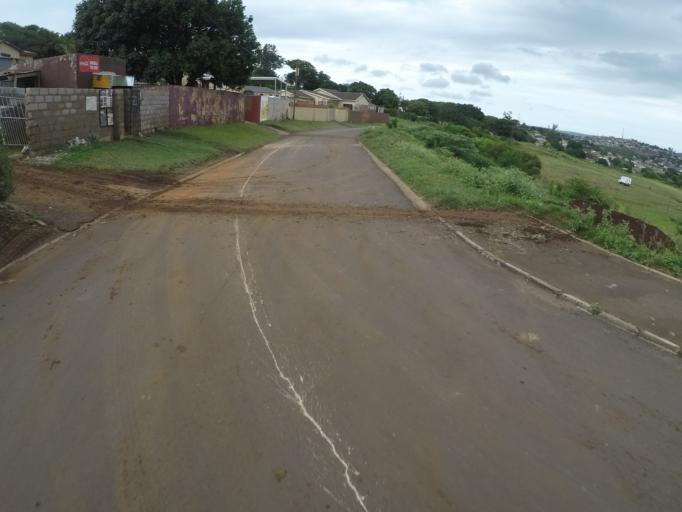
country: ZA
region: KwaZulu-Natal
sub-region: uThungulu District Municipality
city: Empangeni
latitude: -28.7698
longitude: 31.8612
